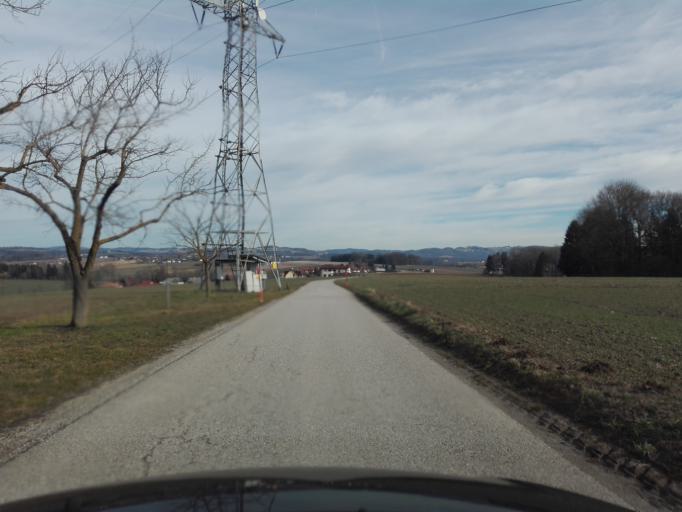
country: AT
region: Lower Austria
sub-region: Politischer Bezirk Amstetten
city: Ennsdorf
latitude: 48.2668
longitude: 14.5334
